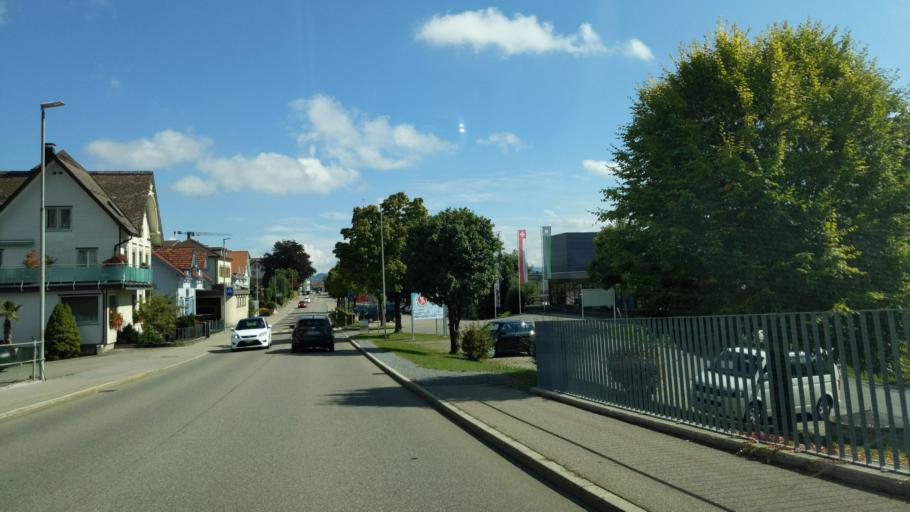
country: CH
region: Appenzell Ausserrhoden
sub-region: Bezirk Hinterland
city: Waldstatt
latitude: 47.3555
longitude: 9.2804
